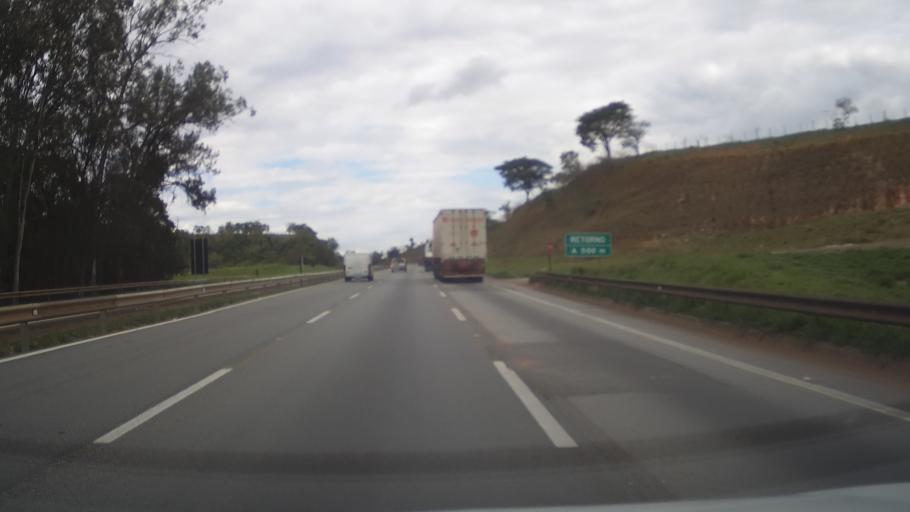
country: BR
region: Minas Gerais
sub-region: Itauna
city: Itauna
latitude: -20.3487
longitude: -44.4437
